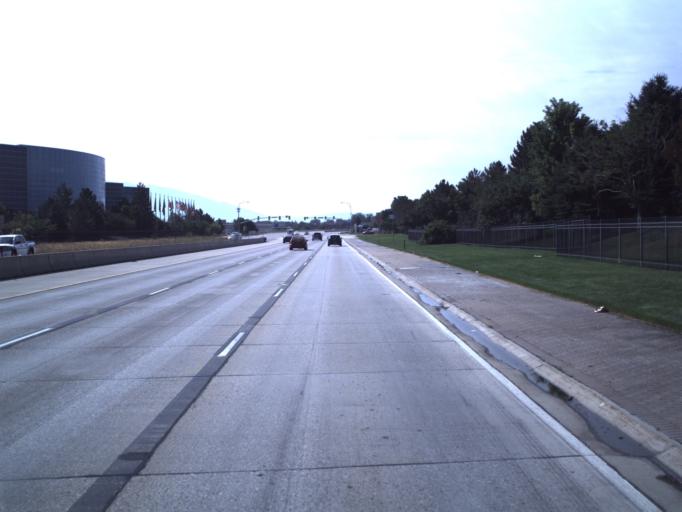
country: US
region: Utah
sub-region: Salt Lake County
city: West Valley City
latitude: 40.7143
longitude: -111.9834
